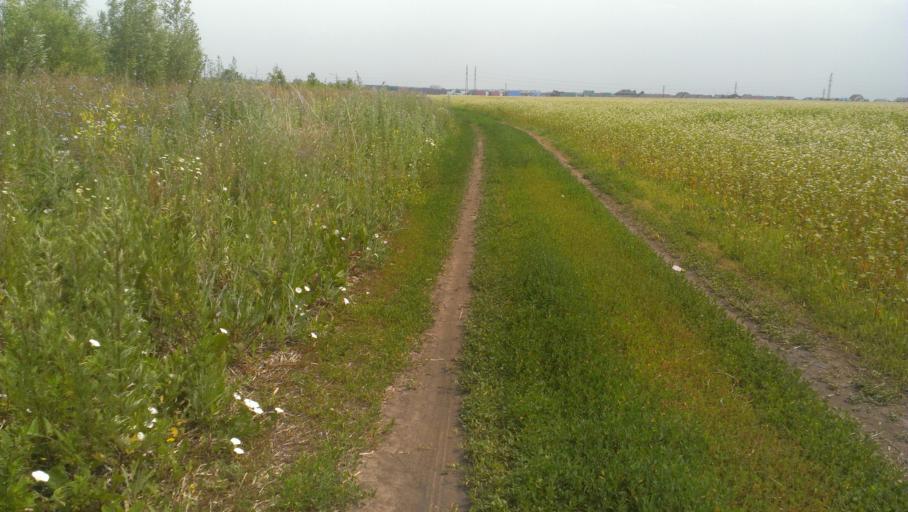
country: RU
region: Altai Krai
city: Novosilikatnyy
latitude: 53.3762
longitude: 83.6420
